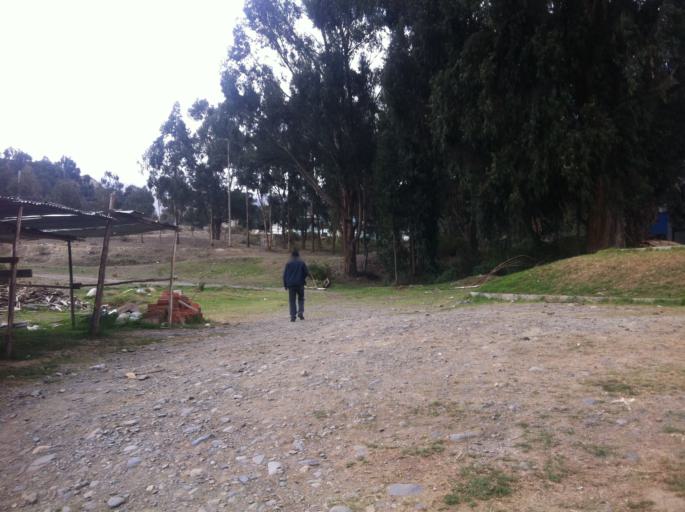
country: BO
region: La Paz
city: La Paz
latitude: -16.5384
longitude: -68.0659
